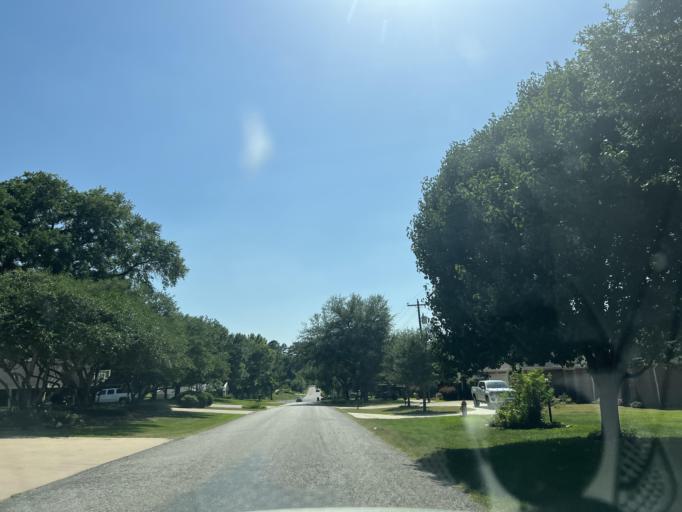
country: US
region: Texas
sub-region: Washington County
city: Brenham
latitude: 30.1530
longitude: -96.3657
